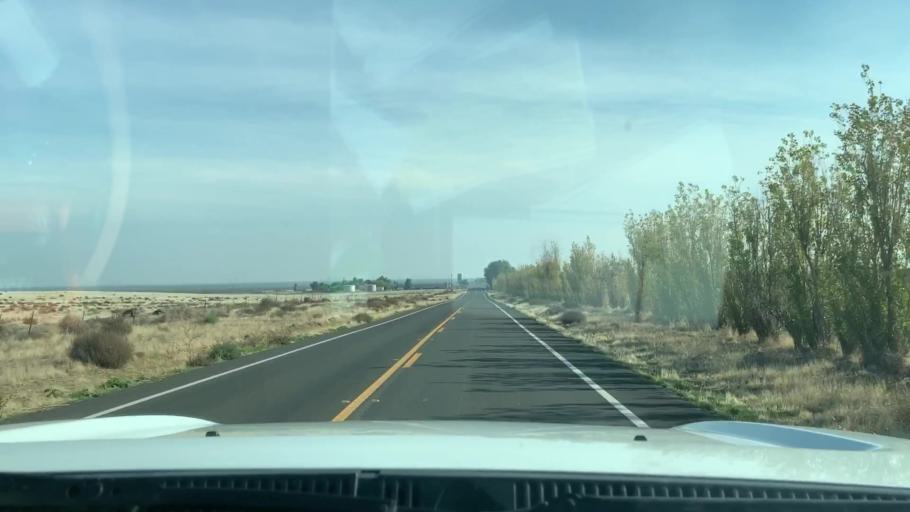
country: US
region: California
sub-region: Fresno County
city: Coalinga
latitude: 36.2541
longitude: -120.2626
